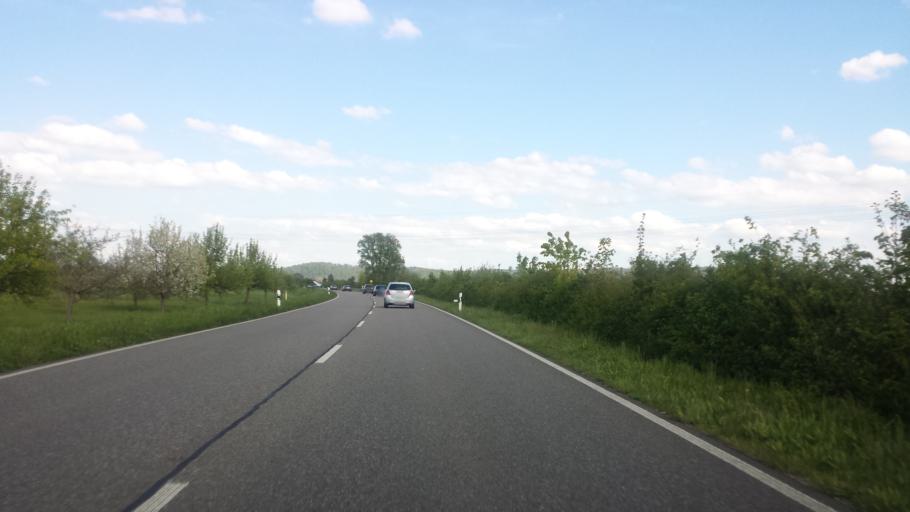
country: DE
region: Baden-Wuerttemberg
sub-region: Karlsruhe Region
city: Karlsdorf-Neuthard
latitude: 49.1038
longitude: 8.5126
